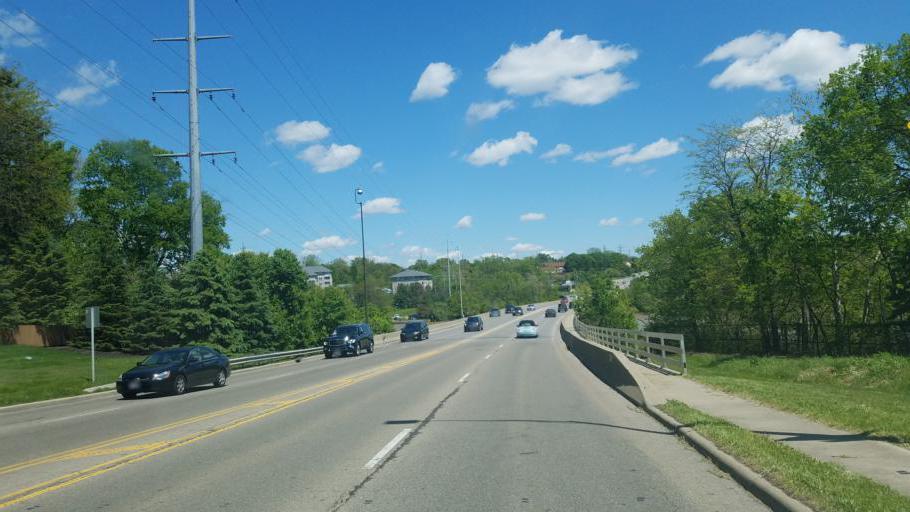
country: US
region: Ohio
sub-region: Franklin County
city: Dublin
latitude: 40.0678
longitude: -83.1092
